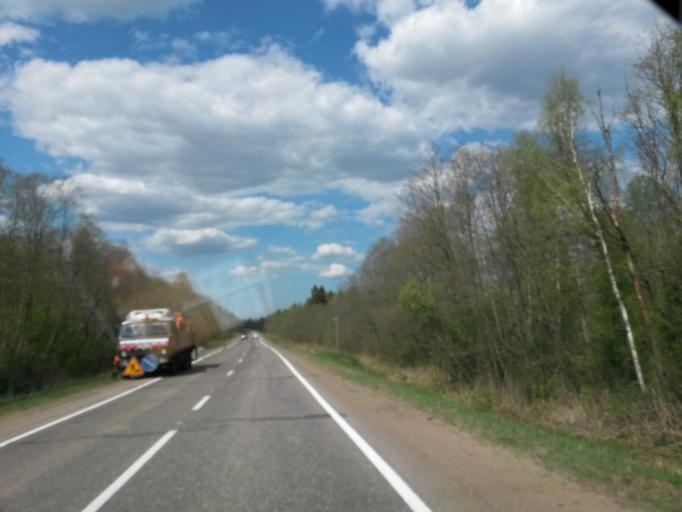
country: RU
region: Jaroslavl
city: Bol'shoye Selo
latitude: 57.6919
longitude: 39.1946
